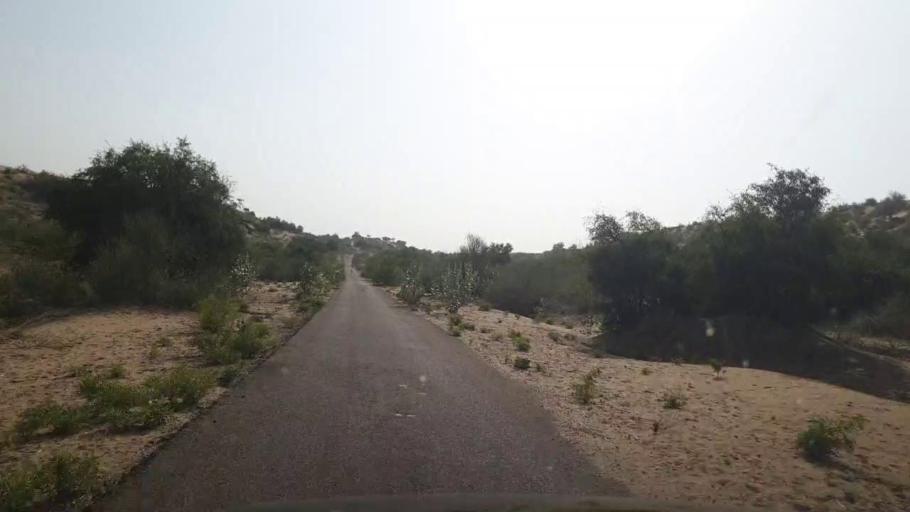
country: PK
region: Sindh
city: Islamkot
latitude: 25.1129
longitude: 70.5074
